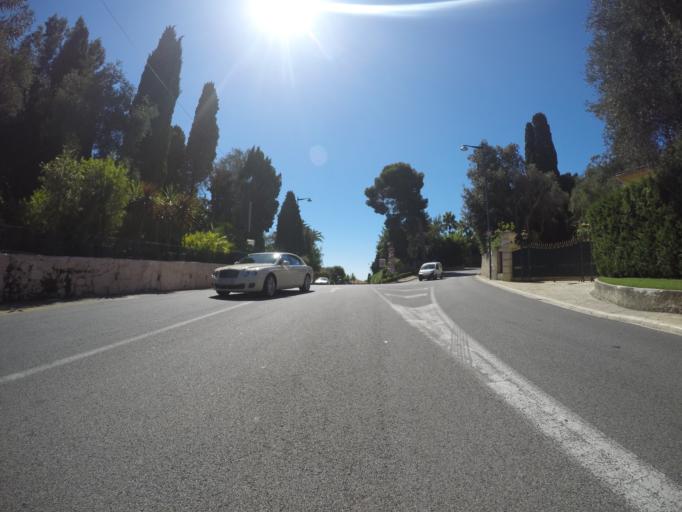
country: FR
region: Provence-Alpes-Cote d'Azur
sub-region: Departement des Alpes-Maritimes
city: Saint-Jean-Cap-Ferrat
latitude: 43.6923
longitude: 7.3287
